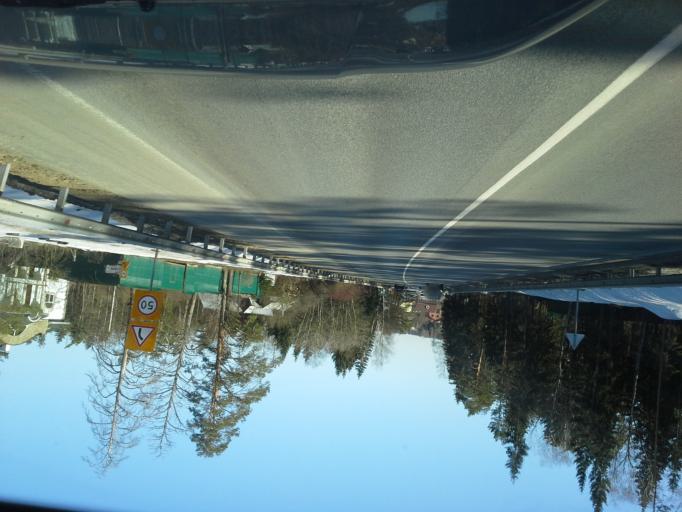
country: RU
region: Moskovskaya
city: Gorki Vtoryye
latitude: 55.6795
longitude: 37.1614
